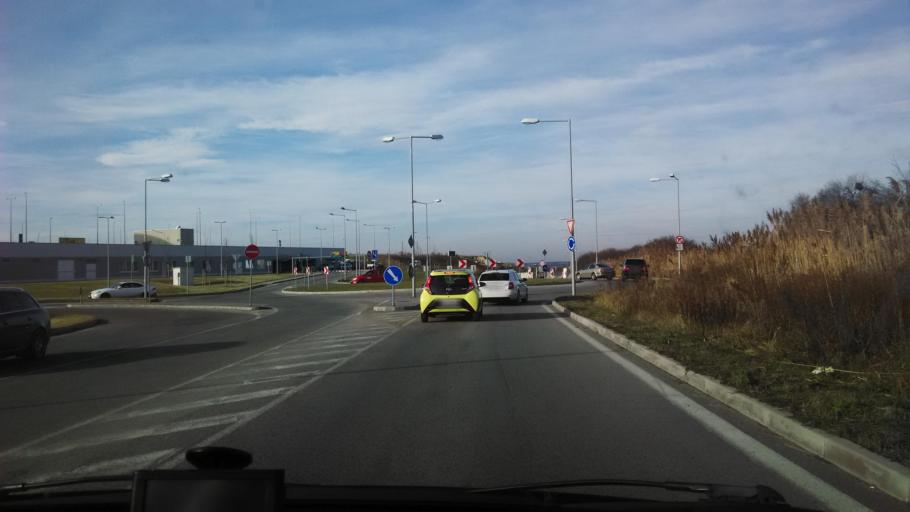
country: SK
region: Bratislavsky
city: Stupava
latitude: 48.2068
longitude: 17.0350
